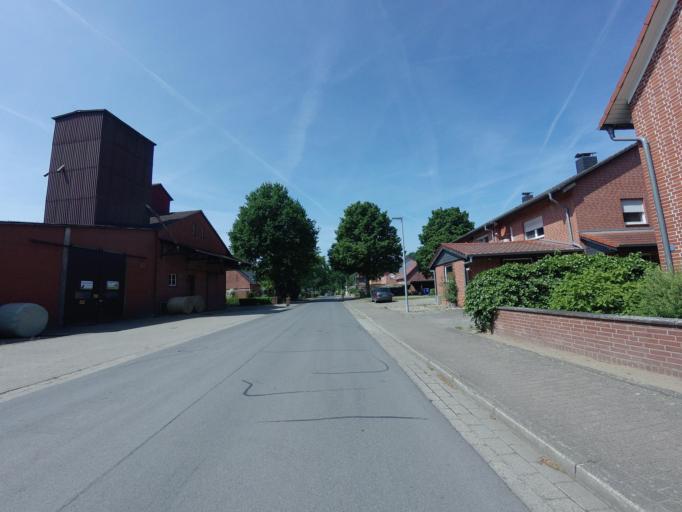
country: DE
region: Lower Saxony
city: Adenbuettel
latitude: 52.3815
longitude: 10.4561
